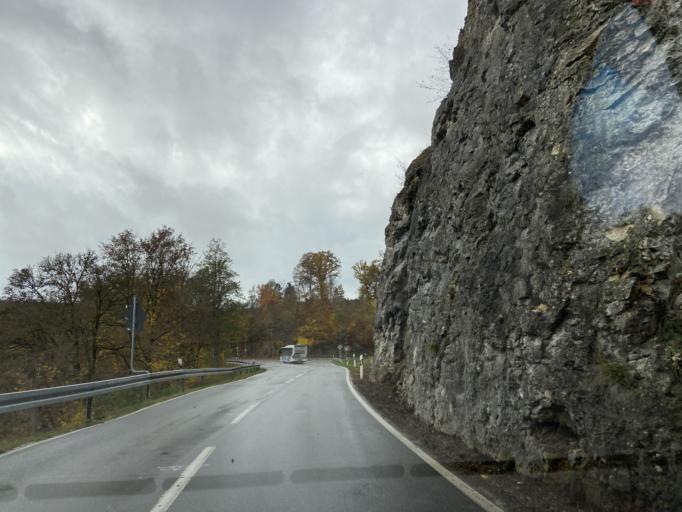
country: DE
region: Baden-Wuerttemberg
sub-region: Tuebingen Region
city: Stetten am Kalten Markt
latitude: 48.0917
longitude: 9.0996
